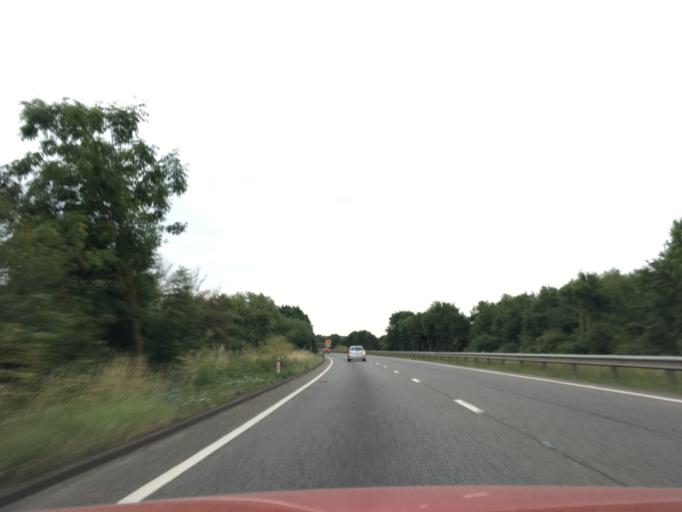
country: GB
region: England
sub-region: Milton Keynes
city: Water Eaton
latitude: 51.9984
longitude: -0.7074
